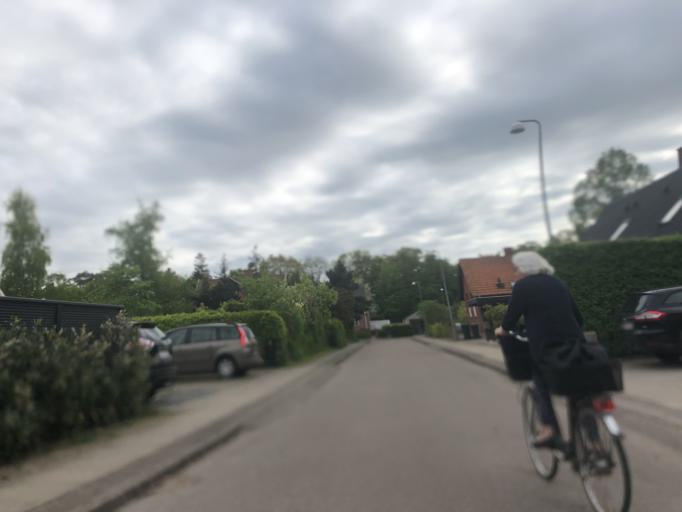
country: DK
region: Zealand
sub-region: Koge Kommune
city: Koge
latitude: 55.4548
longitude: 12.1772
